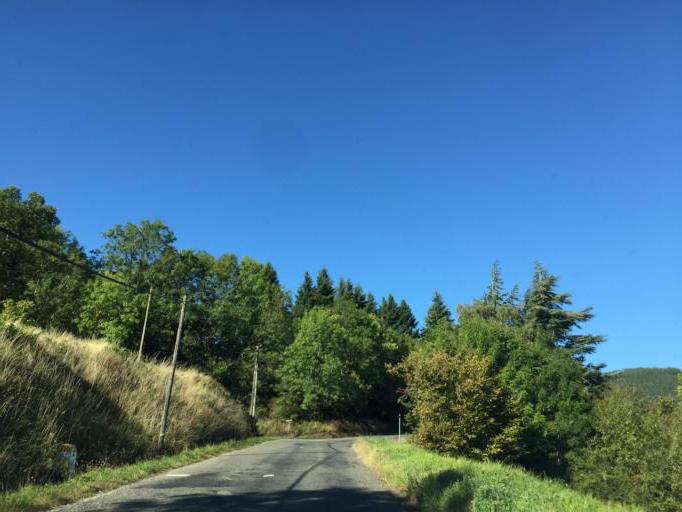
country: FR
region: Rhone-Alpes
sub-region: Departement de la Loire
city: Saint-Paul-en-Jarez
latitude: 45.4285
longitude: 4.5746
